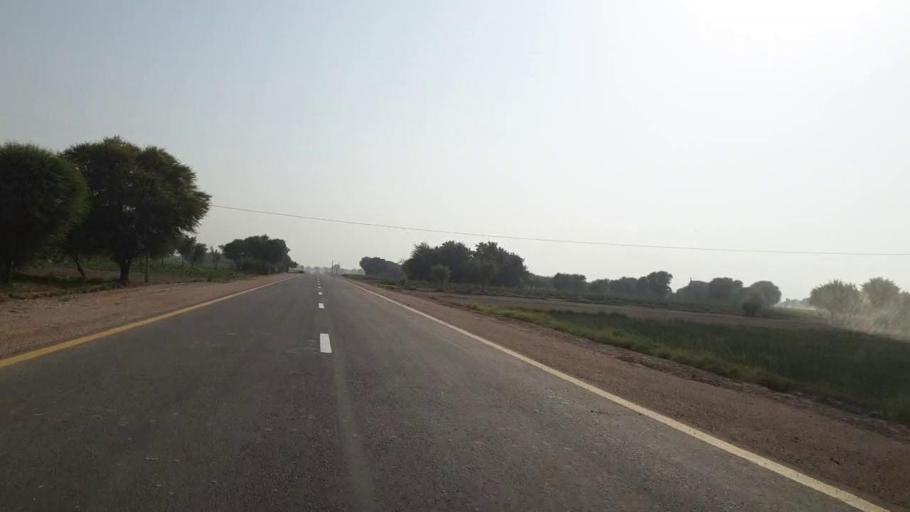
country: PK
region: Sindh
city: Bhan
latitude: 26.5205
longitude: 67.7877
